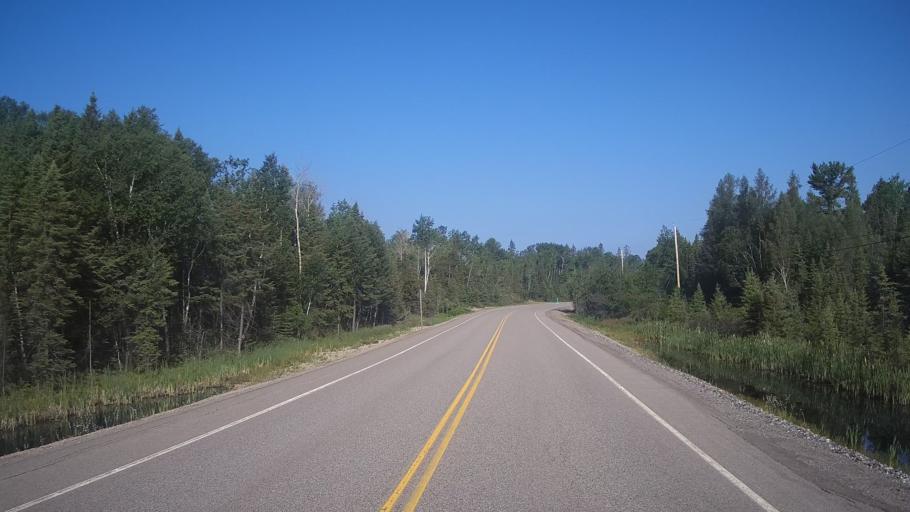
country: CA
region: Ontario
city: Rayside-Balfour
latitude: 46.7311
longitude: -81.5859
